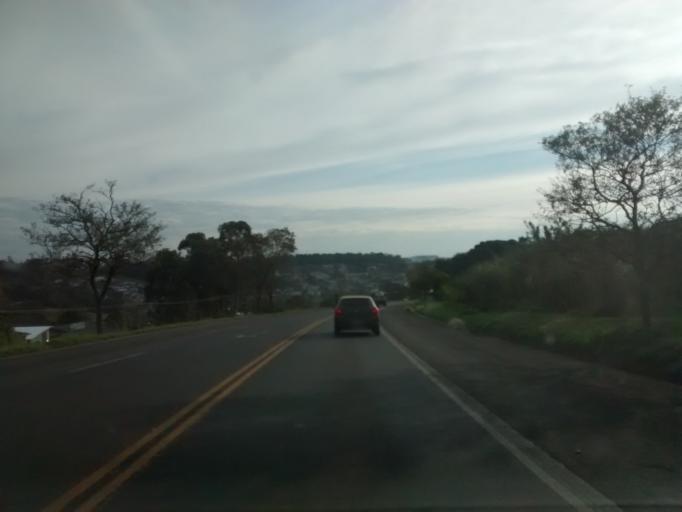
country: BR
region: Parana
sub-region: Pato Branco
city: Pato Branco
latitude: -26.2276
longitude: -52.6896
